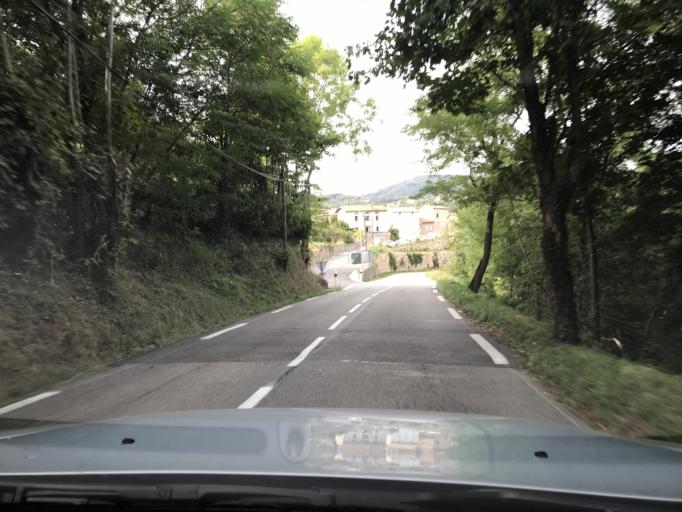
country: FR
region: Rhone-Alpes
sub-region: Departement de l'Ardeche
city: Lamastre
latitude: 44.9834
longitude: 4.5853
